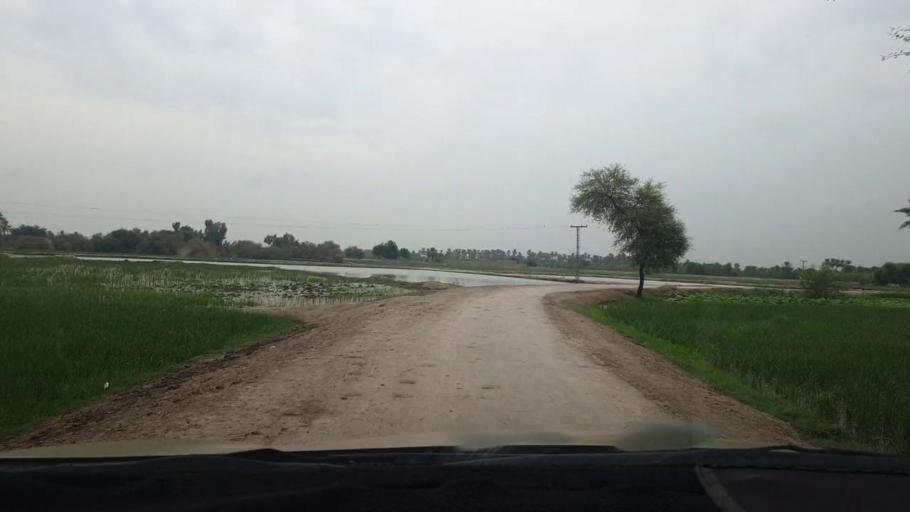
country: PK
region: Sindh
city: Larkana
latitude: 27.5746
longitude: 68.2438
